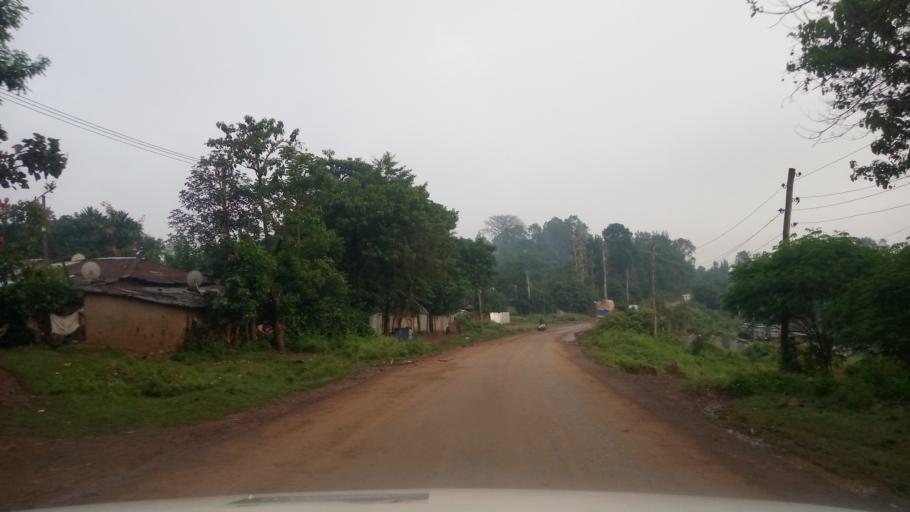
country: ET
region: Oromiya
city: Jima
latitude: 7.6885
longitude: 36.8269
